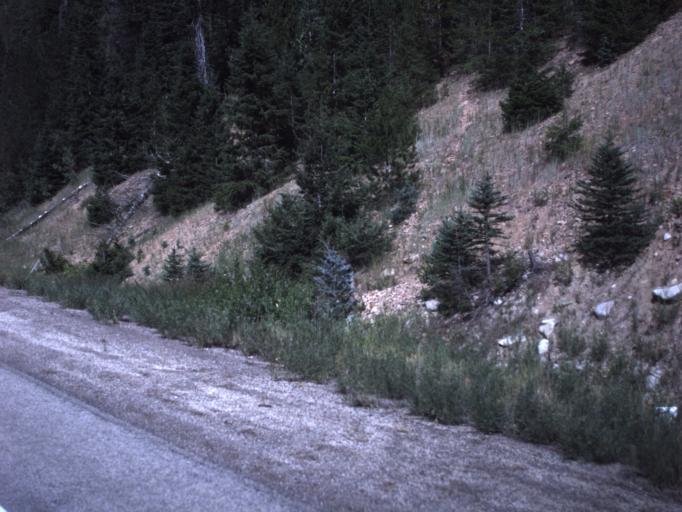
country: US
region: Utah
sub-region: Wasatch County
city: Heber
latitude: 40.3264
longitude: -111.2617
